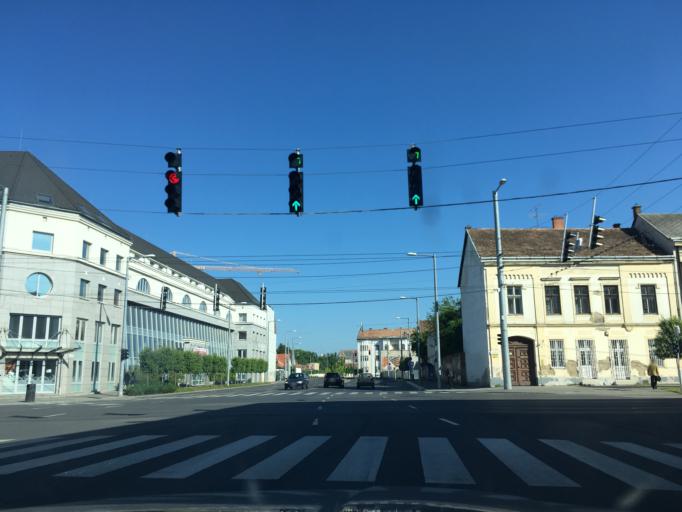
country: HU
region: Hajdu-Bihar
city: Debrecen
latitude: 47.5273
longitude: 21.6212
